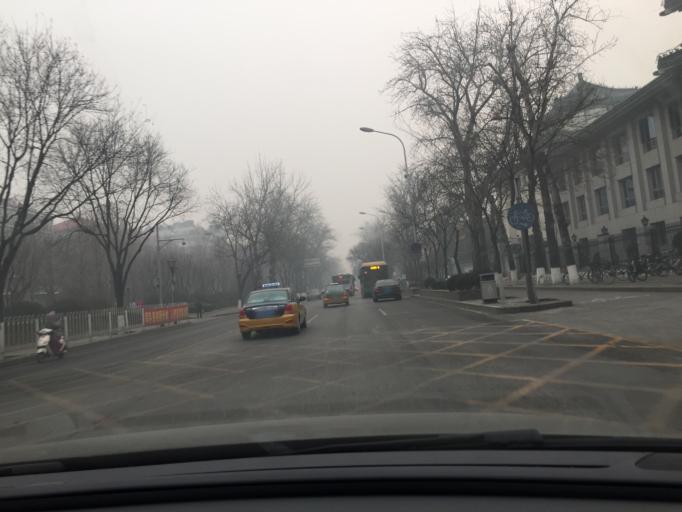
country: CN
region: Beijing
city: Jingshan
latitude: 39.9167
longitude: 116.4003
